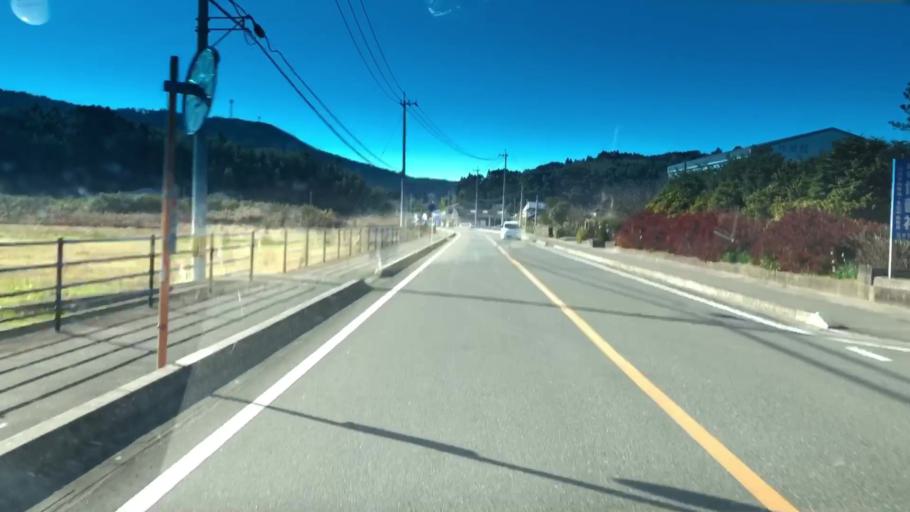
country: JP
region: Kagoshima
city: Satsumasendai
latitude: 31.8173
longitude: 130.2799
